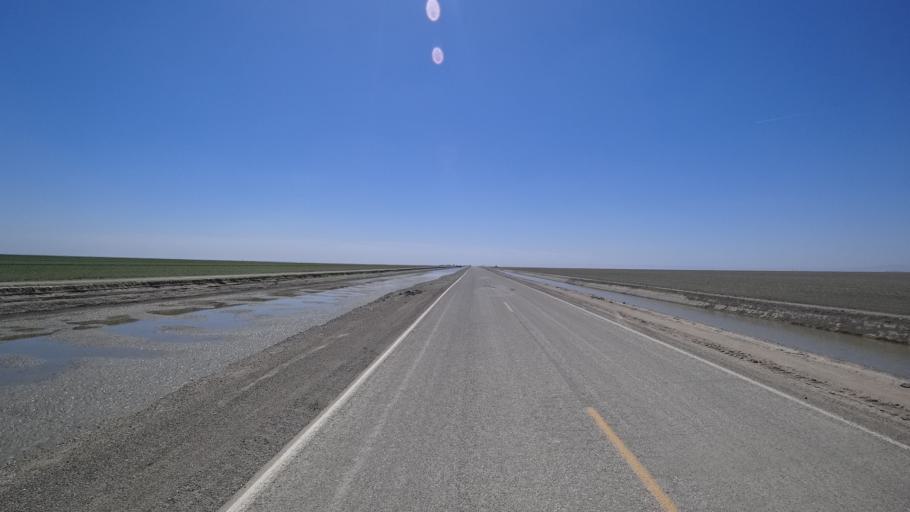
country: US
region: California
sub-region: Kings County
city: Corcoran
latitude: 36.0061
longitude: -119.6432
